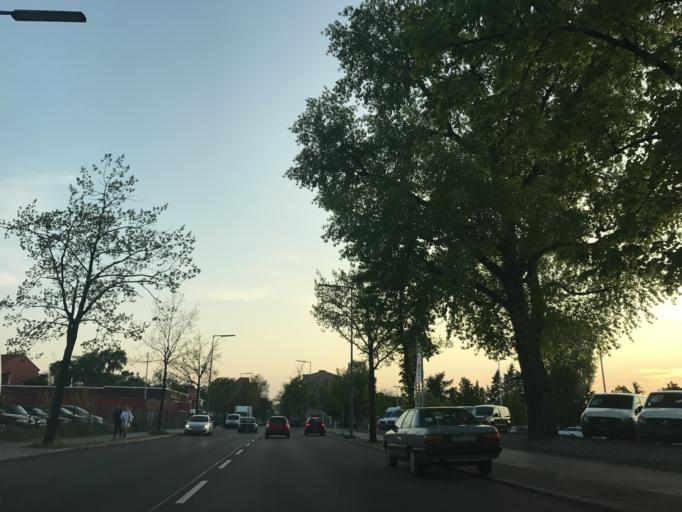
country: DE
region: Berlin
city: Wilhelmstadt
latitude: 52.5271
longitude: 13.1852
